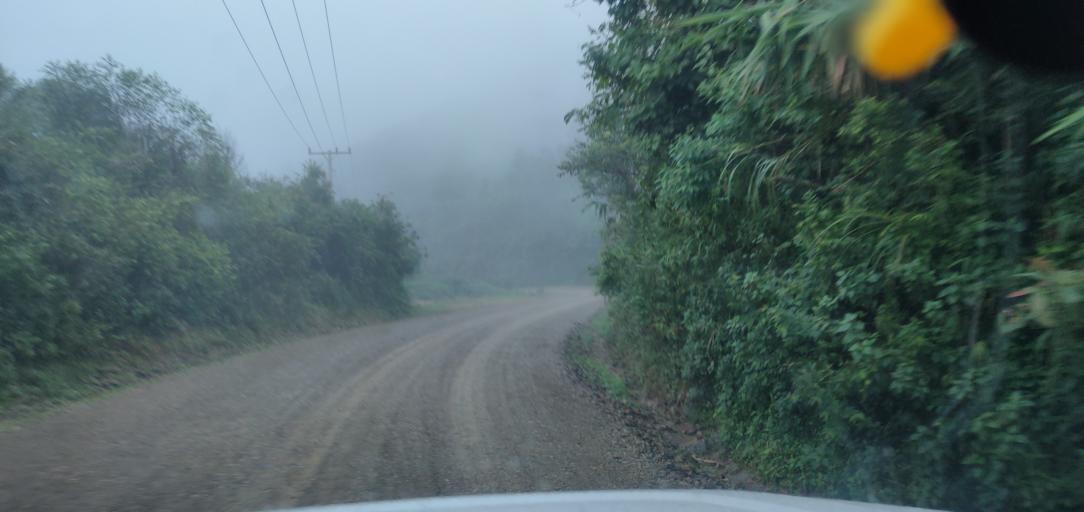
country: LA
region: Phongsali
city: Phongsali
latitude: 21.3912
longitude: 102.2021
